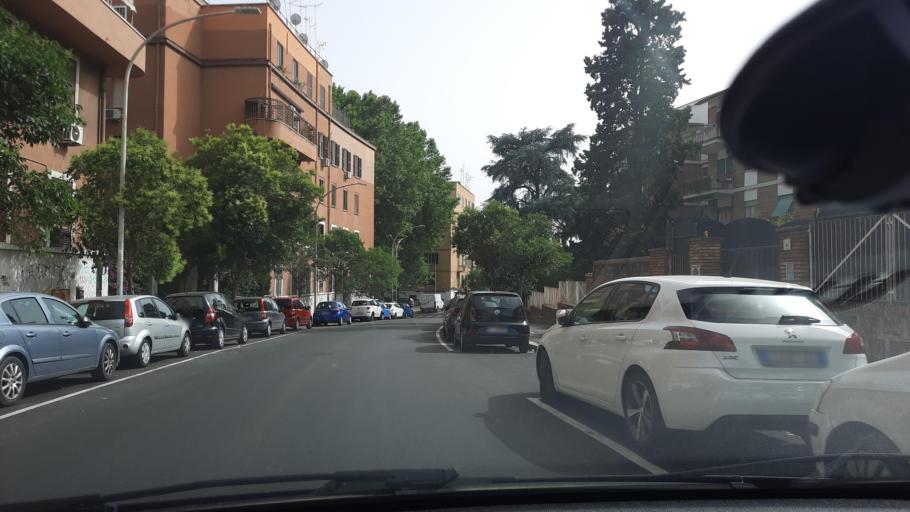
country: IT
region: Latium
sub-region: Citta metropolitana di Roma Capitale
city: Rome
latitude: 41.8592
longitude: 12.4899
